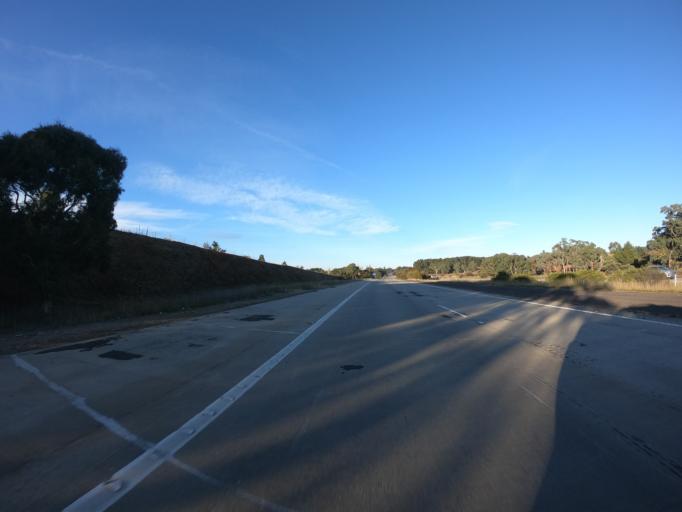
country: AU
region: New South Wales
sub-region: Yass Valley
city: Gundaroo
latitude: -35.1374
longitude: 149.3386
